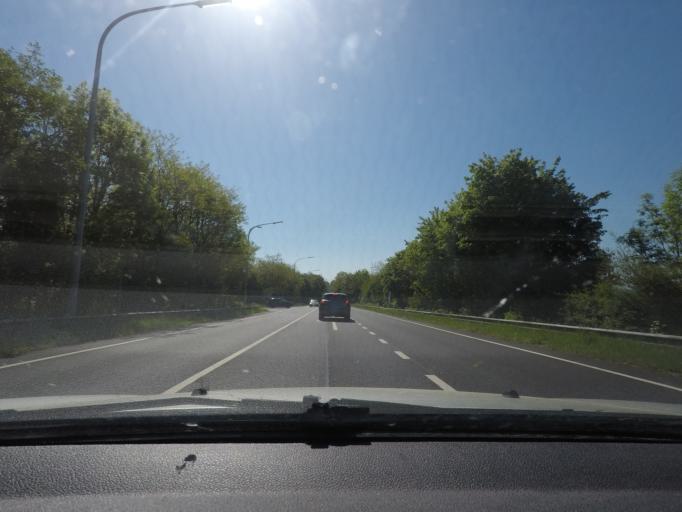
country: BE
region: Wallonia
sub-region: Province de Namur
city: Houyet
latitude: 50.1660
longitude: 5.0748
